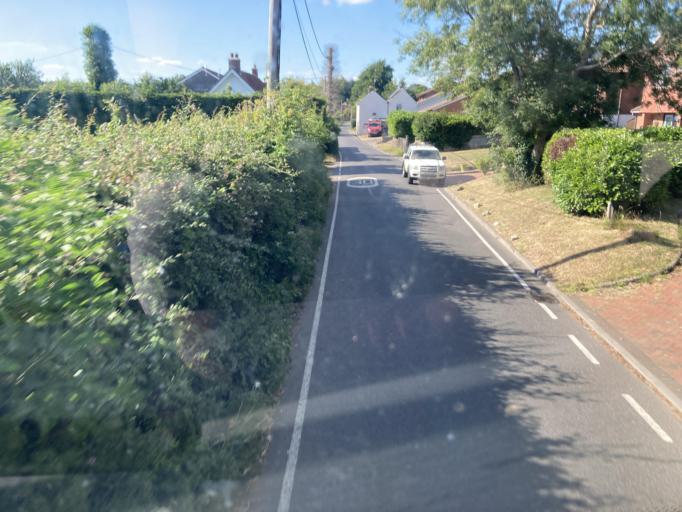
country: GB
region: England
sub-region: Isle of Wight
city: Newchurch
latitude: 50.6604
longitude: -1.2546
